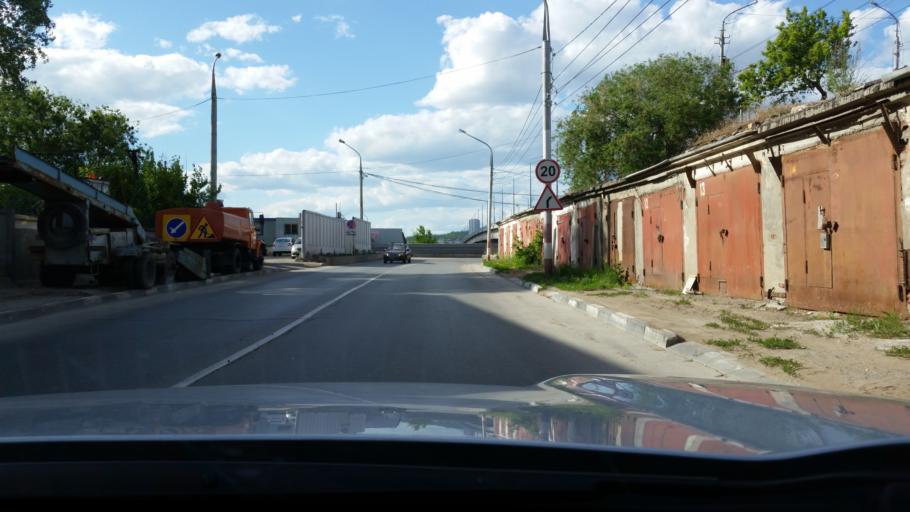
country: RU
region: Saratov
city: Engel's
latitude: 51.5051
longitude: 46.0780
